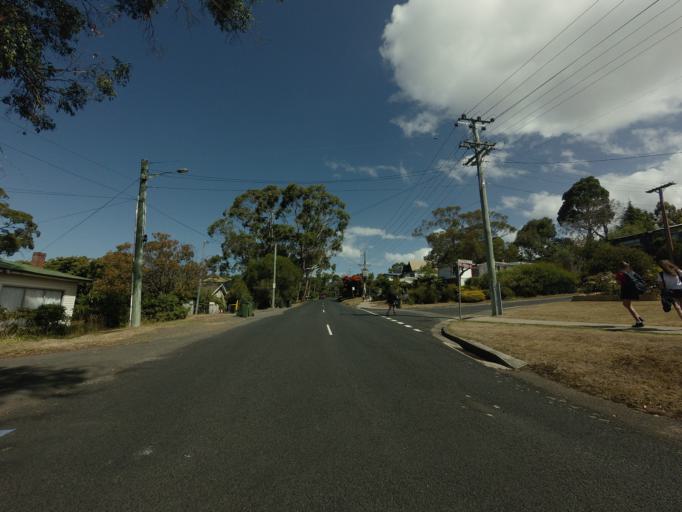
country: AU
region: Tasmania
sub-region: Hobart
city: Dynnyrne
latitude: -42.9156
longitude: 147.3241
